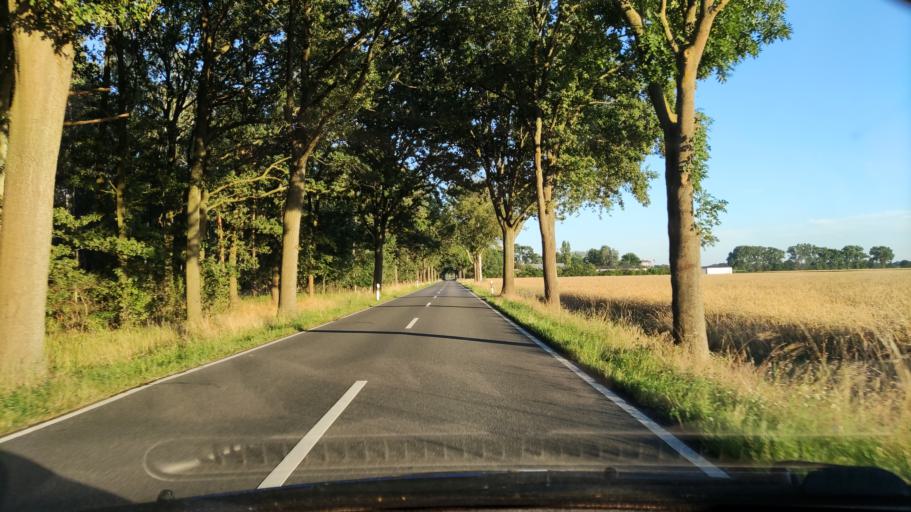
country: DE
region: Lower Saxony
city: Luechow
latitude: 53.0197
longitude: 11.1464
